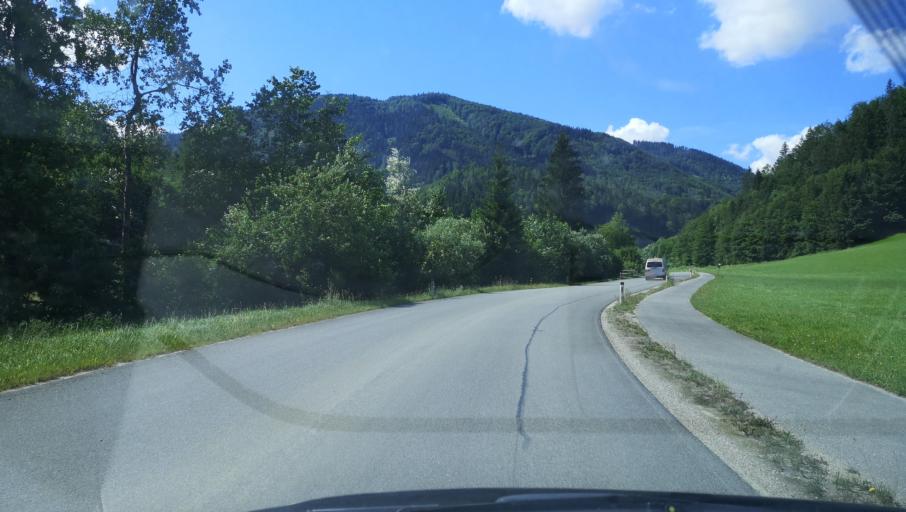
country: AT
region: Lower Austria
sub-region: Politischer Bezirk Scheibbs
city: Gresten
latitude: 47.9357
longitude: 15.0284
